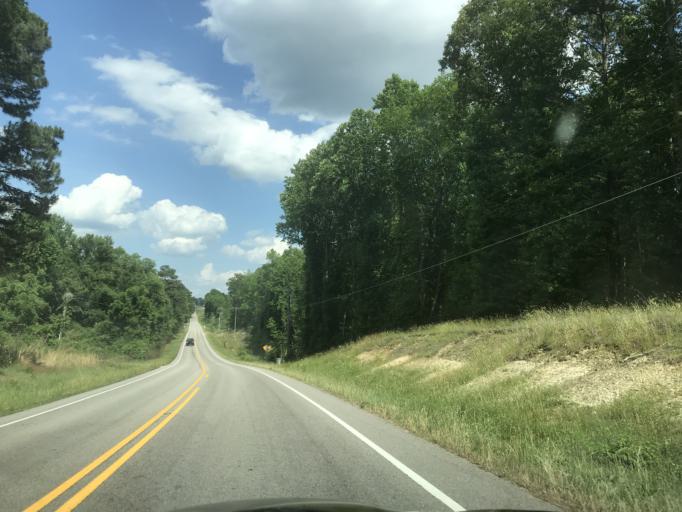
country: US
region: North Carolina
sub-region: Wake County
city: Zebulon
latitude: 35.9587
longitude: -78.2744
